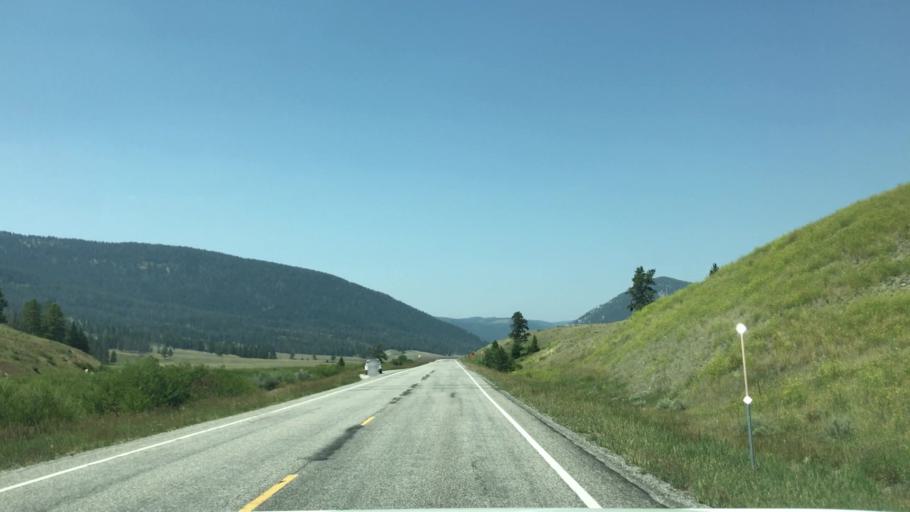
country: US
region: Montana
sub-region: Gallatin County
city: Big Sky
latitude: 45.0405
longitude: -111.1242
